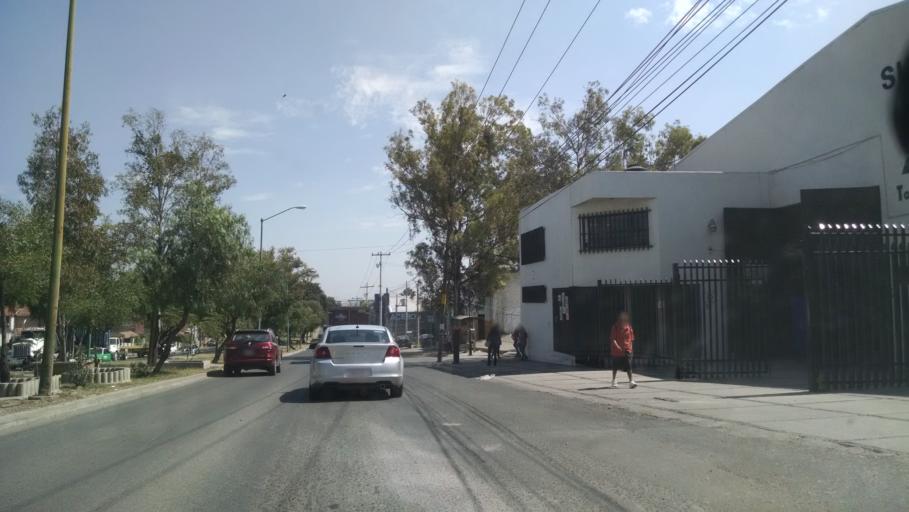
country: MX
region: Guanajuato
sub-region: Leon
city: Ejido la Joya
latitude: 21.1207
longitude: -101.7198
